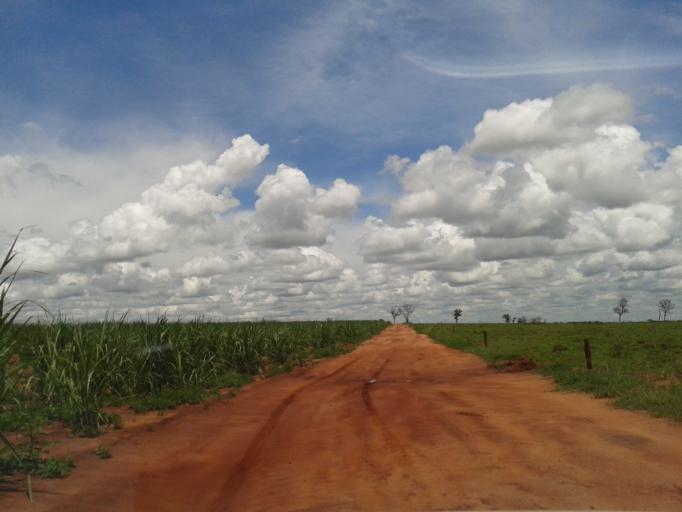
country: BR
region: Minas Gerais
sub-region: Santa Vitoria
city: Santa Vitoria
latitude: -19.2011
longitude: -50.6584
